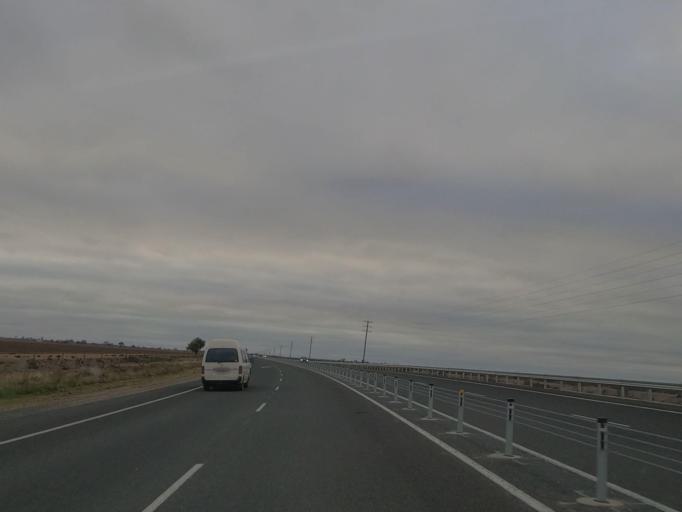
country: AU
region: Victoria
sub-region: Swan Hill
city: Swan Hill
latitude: -35.5095
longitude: 143.7235
